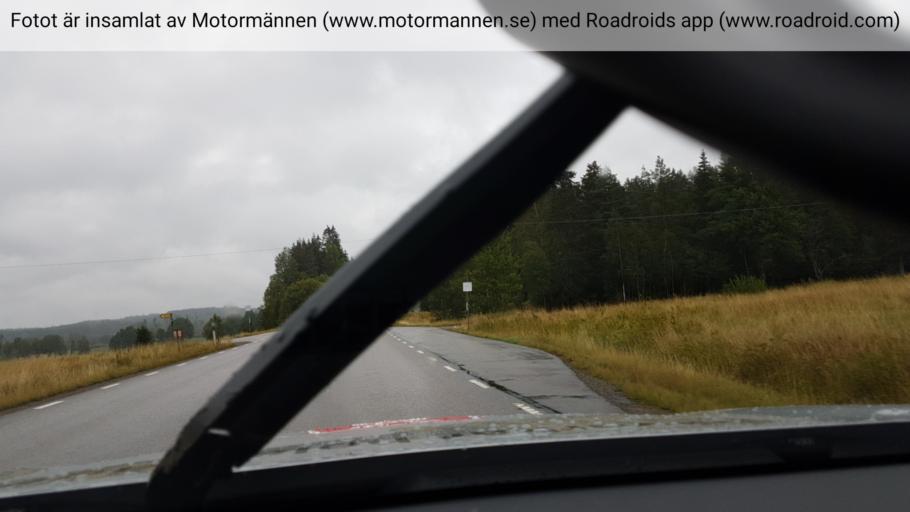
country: SE
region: Vaestra Goetaland
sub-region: Bengtsfors Kommun
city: Billingsfors
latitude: 58.9439
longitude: 12.2129
